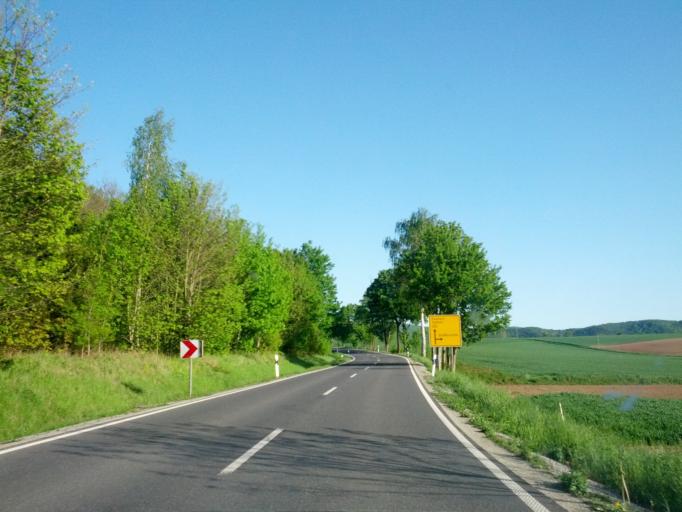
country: DE
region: Thuringia
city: Treffurt
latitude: 51.1466
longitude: 10.1939
